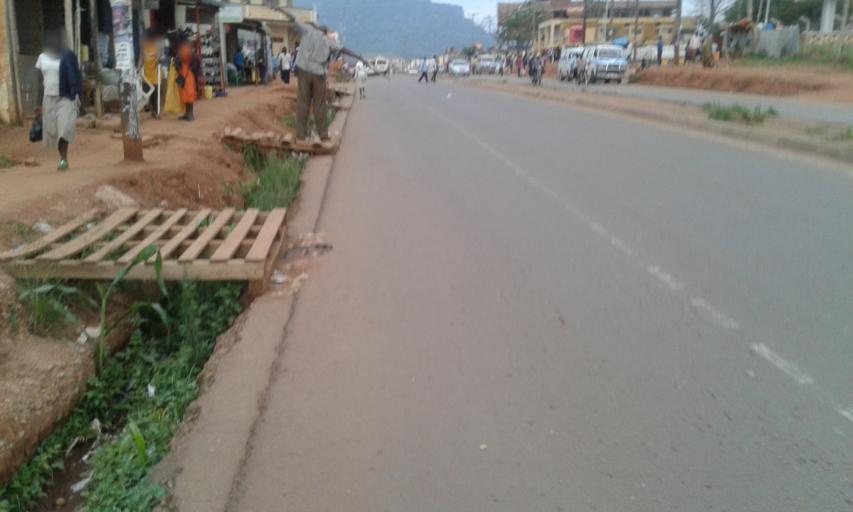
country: UG
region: Eastern Region
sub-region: Mbale District
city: Mbale
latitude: 1.0770
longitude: 34.1747
